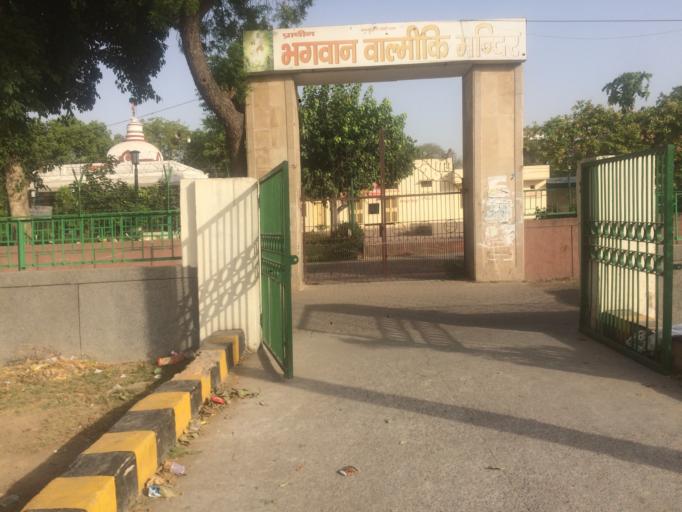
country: IN
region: NCT
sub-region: Central Delhi
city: Karol Bagh
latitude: 28.6406
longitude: 77.2035
